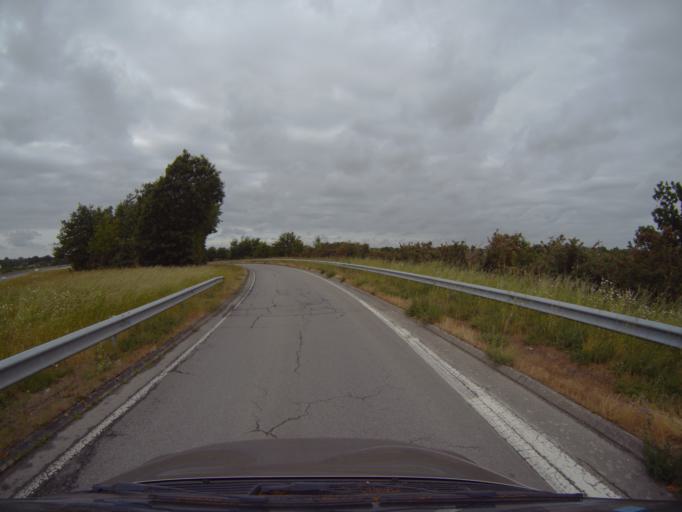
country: FR
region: Pays de la Loire
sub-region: Departement de la Loire-Atlantique
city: La Chevroliere
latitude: 47.0621
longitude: -1.5947
